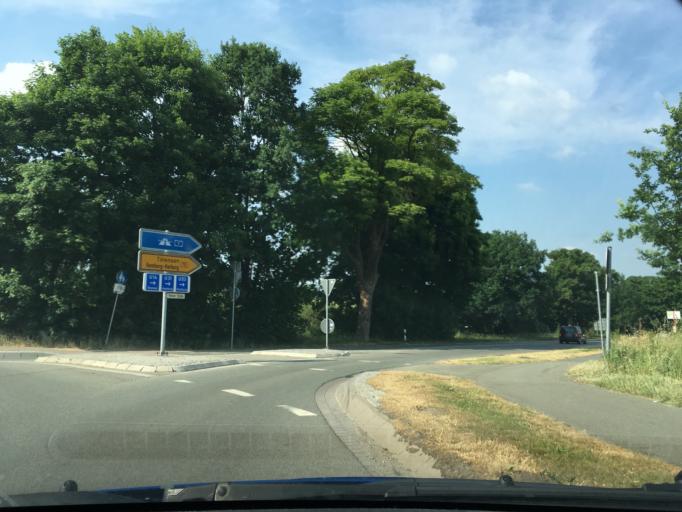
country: DE
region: Lower Saxony
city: Buchholz in der Nordheide
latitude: 53.3754
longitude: 9.8894
